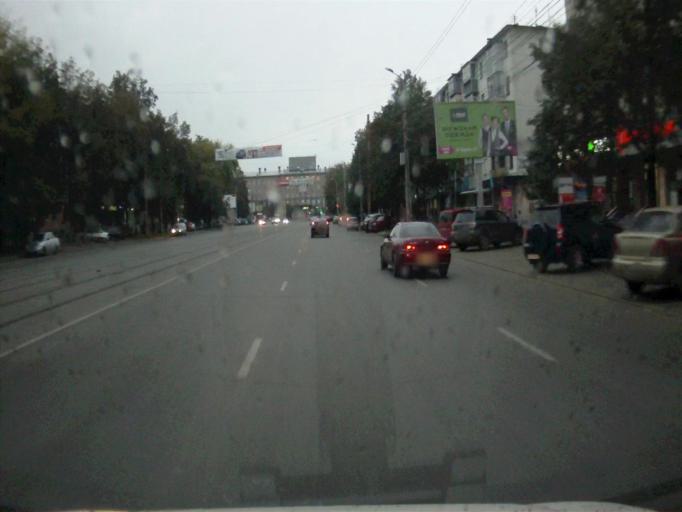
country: RU
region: Chelyabinsk
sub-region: Gorod Chelyabinsk
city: Chelyabinsk
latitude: 55.1807
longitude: 61.3994
